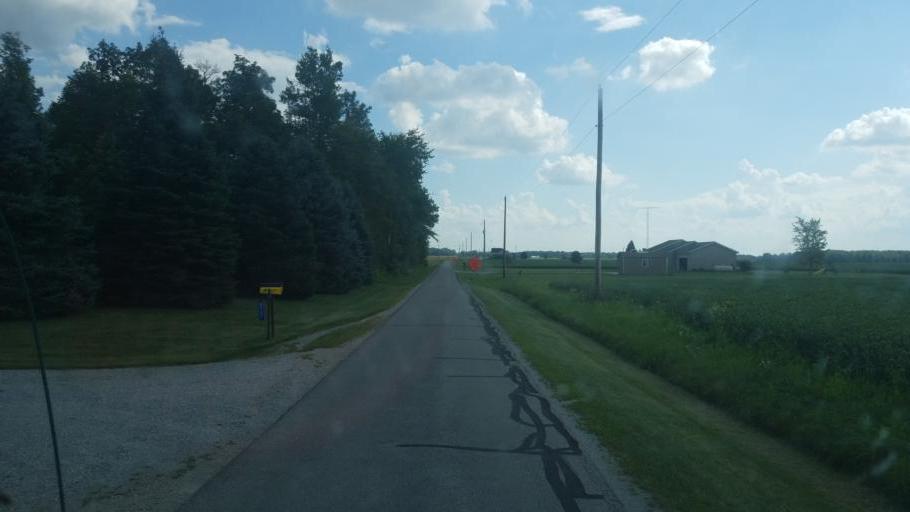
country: US
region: Ohio
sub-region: Huron County
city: Willard
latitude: 40.9978
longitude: -82.8817
